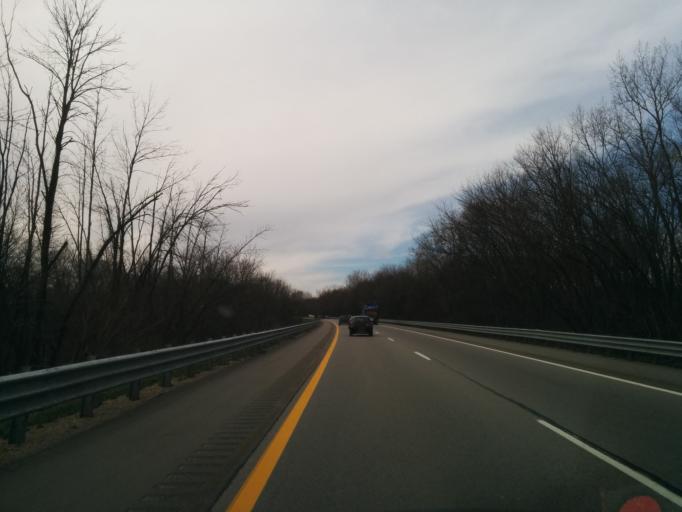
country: US
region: Michigan
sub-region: Kent County
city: Wyoming
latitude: 42.9324
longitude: -85.7324
